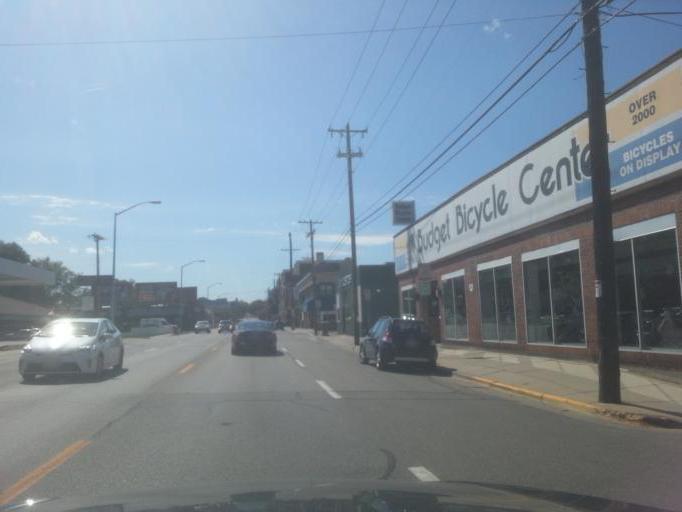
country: US
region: Wisconsin
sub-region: Dane County
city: Madison
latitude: 43.0678
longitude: -89.4065
